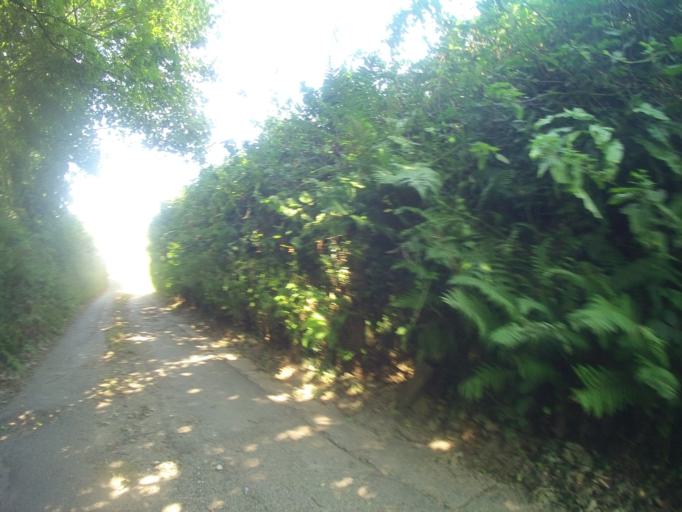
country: GB
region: England
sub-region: Devon
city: Dartmouth
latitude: 50.3635
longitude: -3.6230
